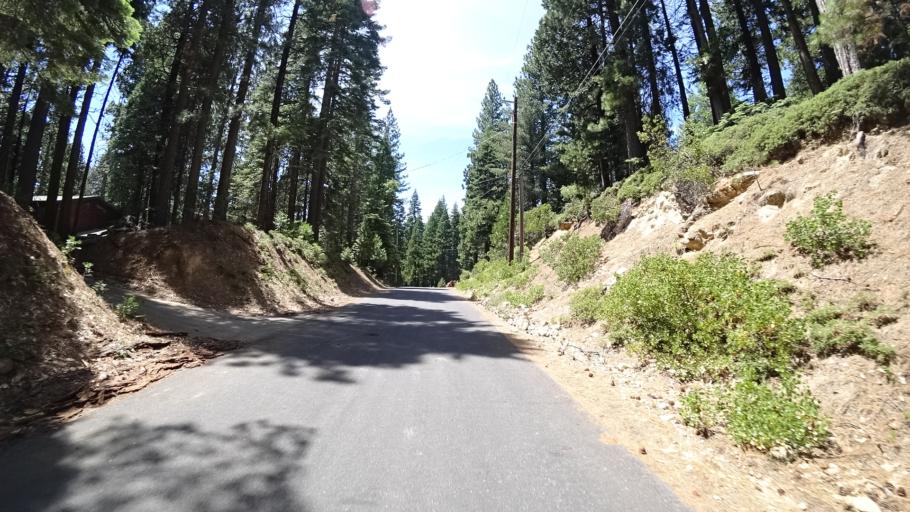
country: US
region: California
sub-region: Calaveras County
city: Arnold
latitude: 38.3040
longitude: -120.2674
